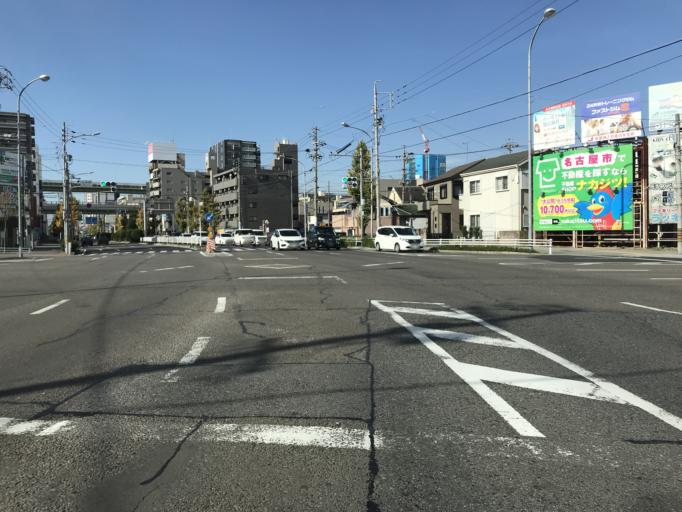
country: JP
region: Aichi
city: Nagoya-shi
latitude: 35.1970
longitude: 136.9154
